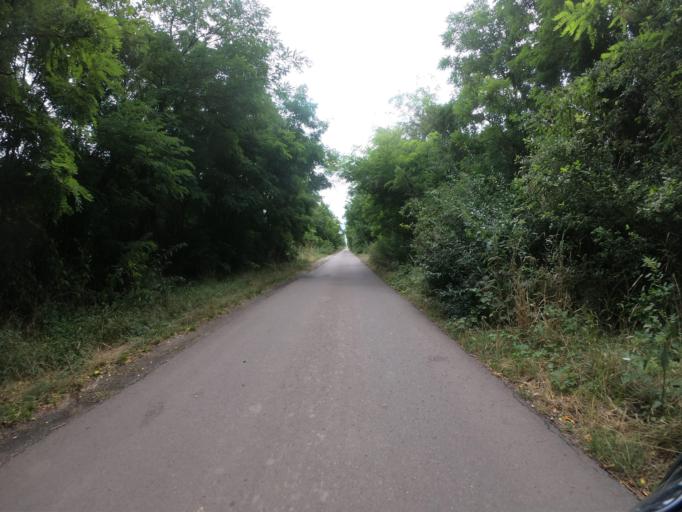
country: HU
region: Borsod-Abauj-Zemplen
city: Szentistvan
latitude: 47.7230
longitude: 20.6867
